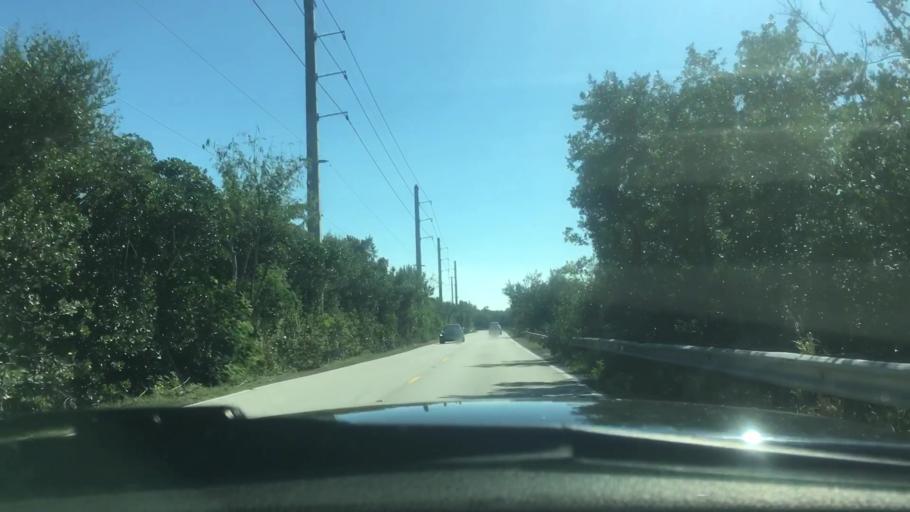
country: US
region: Florida
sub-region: Monroe County
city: North Key Largo
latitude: 25.2945
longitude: -80.3832
